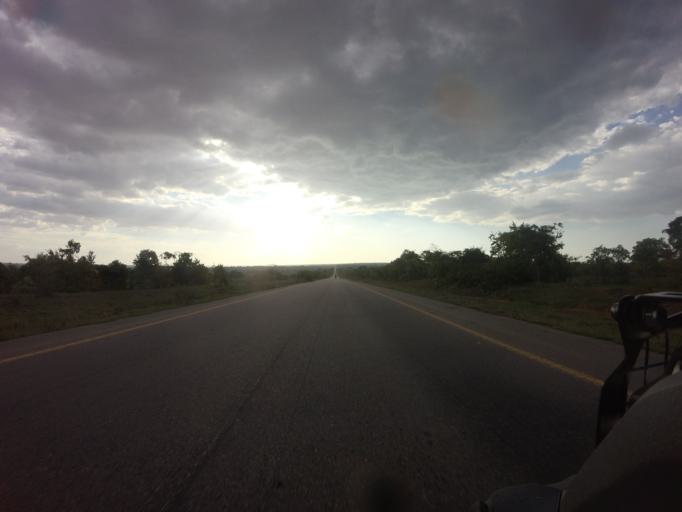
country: AO
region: Huila
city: Lubango
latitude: -14.6028
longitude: 14.0294
